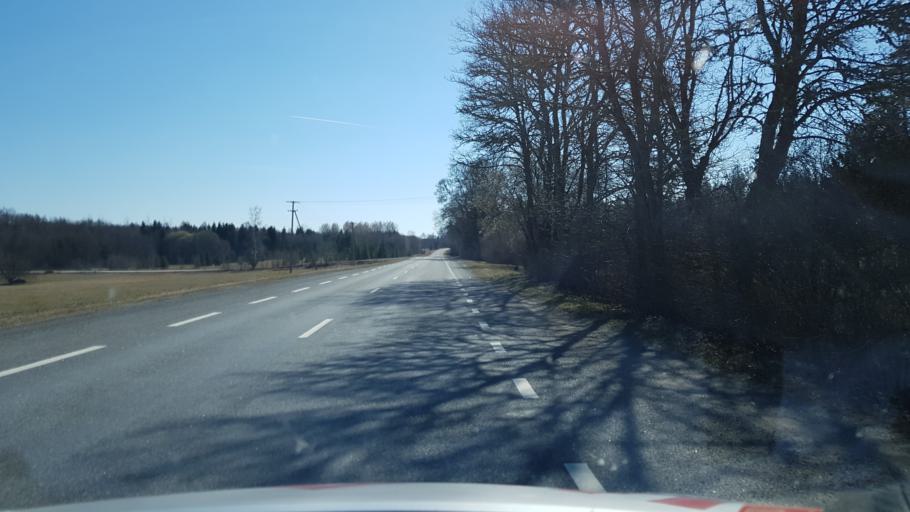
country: EE
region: Jaervamaa
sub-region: Jaerva-Jaani vald
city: Jarva-Jaani
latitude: 59.0679
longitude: 25.9333
